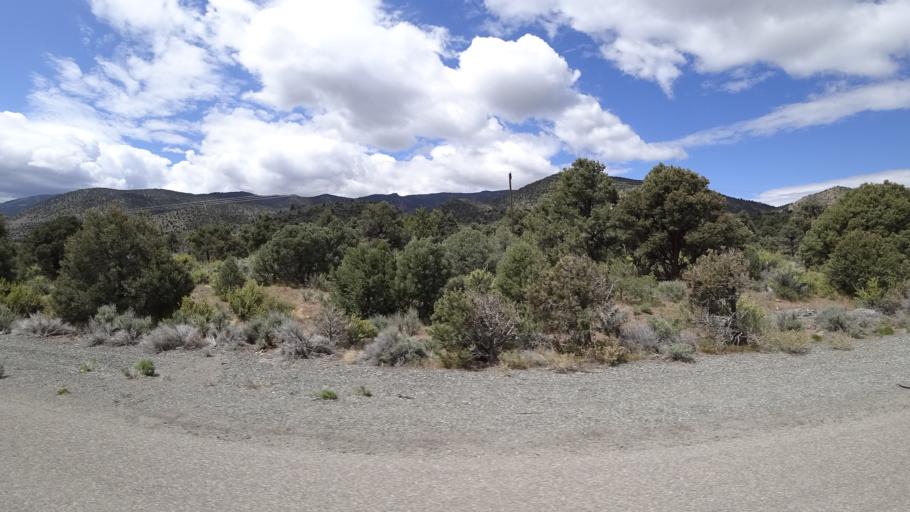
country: US
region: Nevada
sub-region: Douglas County
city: Gardnerville Ranchos
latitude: 38.7542
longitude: -119.5720
